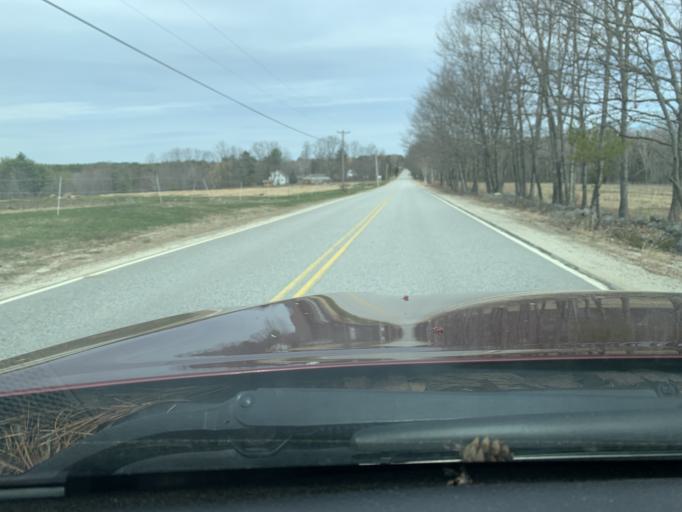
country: US
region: Maine
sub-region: Cumberland County
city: Raymond
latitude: 43.9583
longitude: -70.3889
